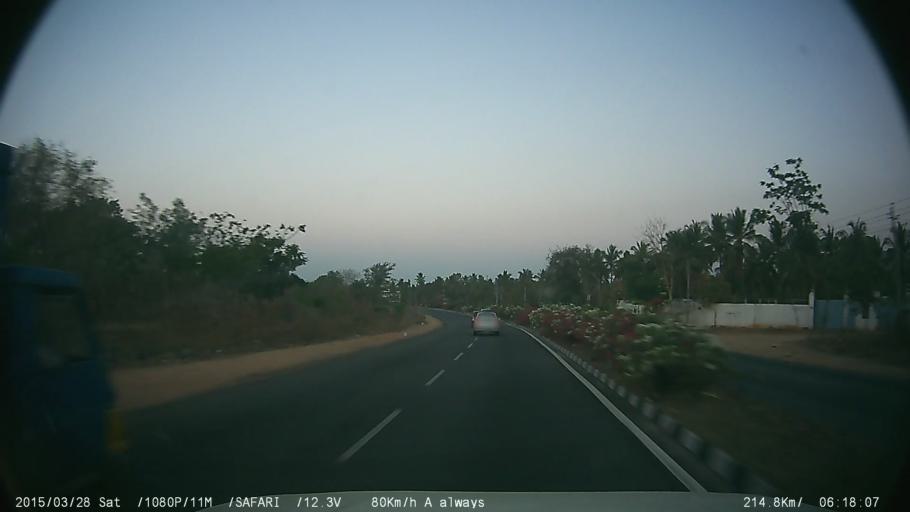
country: IN
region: Karnataka
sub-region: Ramanagara
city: Ramanagaram
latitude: 12.7411
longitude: 77.3078
